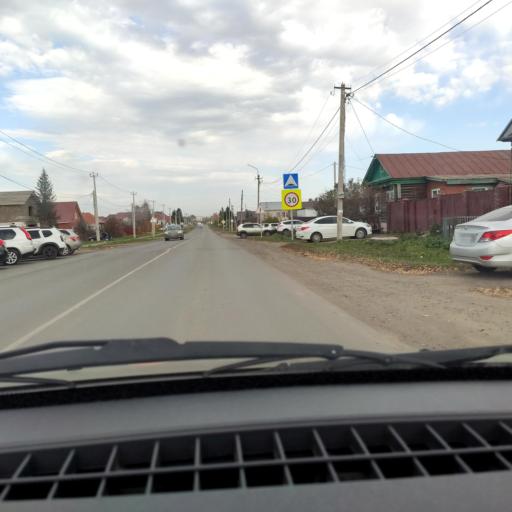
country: RU
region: Bashkortostan
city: Ufa
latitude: 54.6156
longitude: 55.9027
